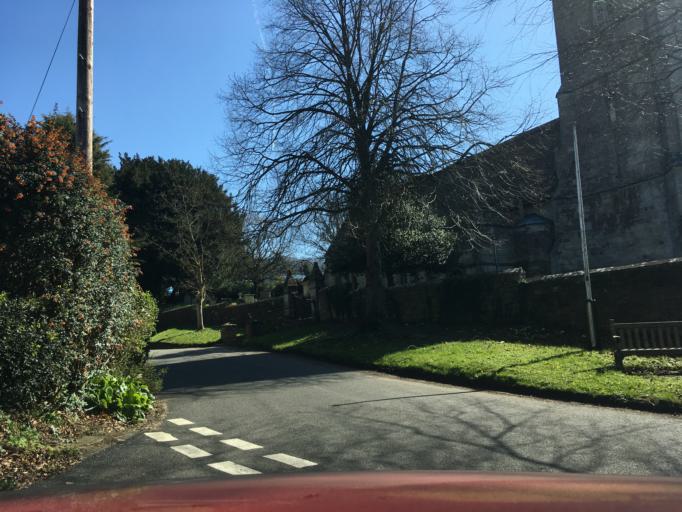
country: GB
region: England
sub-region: Gloucestershire
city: Dursley
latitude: 51.6881
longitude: -2.3931
